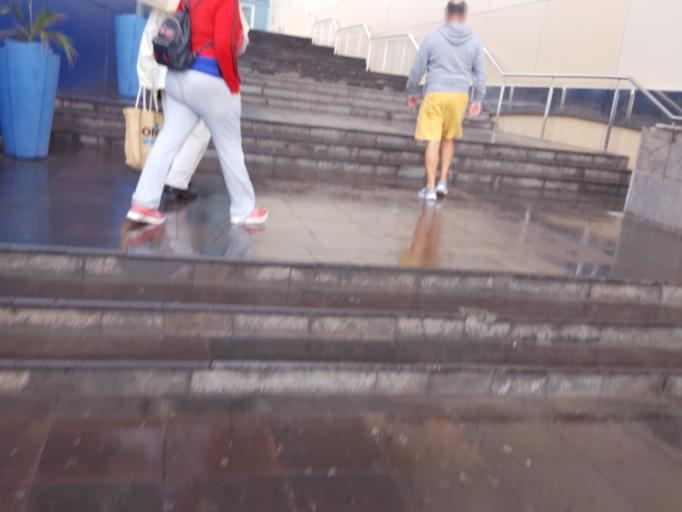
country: ES
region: Canary Islands
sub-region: Provincia de Las Palmas
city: Las Palmas de Gran Canaria
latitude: 28.1412
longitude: -15.4276
